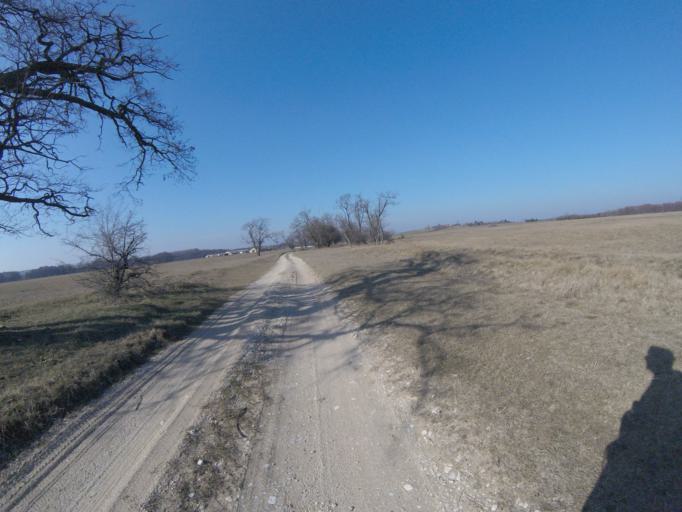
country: HU
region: Komarom-Esztergom
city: Oroszlany
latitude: 47.4674
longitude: 18.3403
